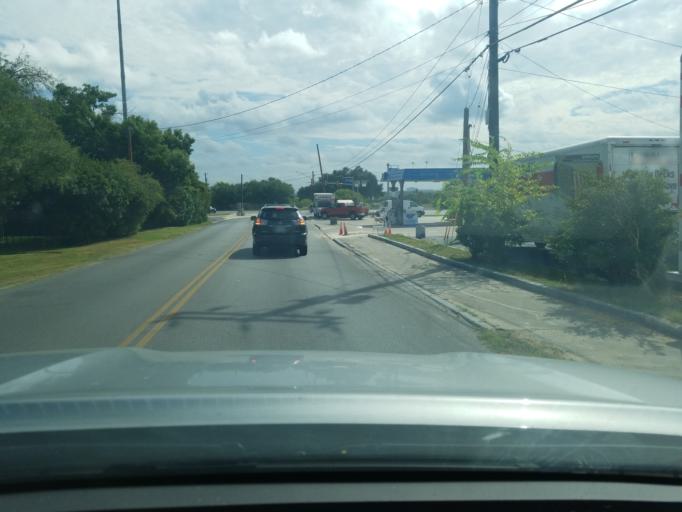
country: US
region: Texas
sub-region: Bexar County
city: Terrell Hills
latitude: 29.4706
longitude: -98.4387
